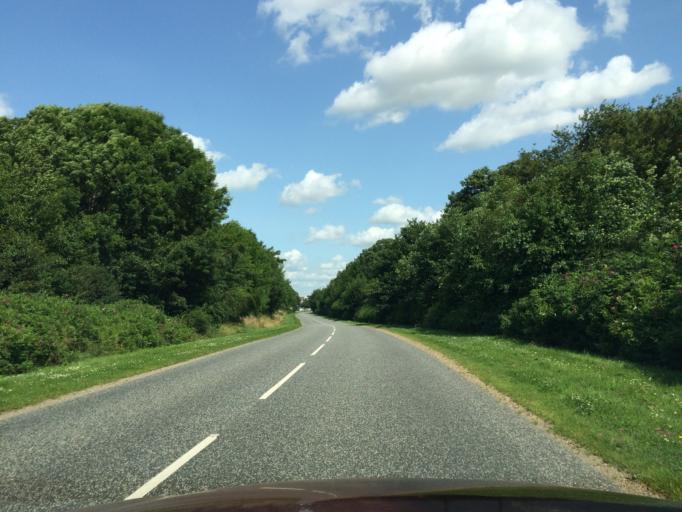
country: DK
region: Central Jutland
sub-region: Viborg Kommune
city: Bjerringbro
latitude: 56.2664
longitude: 9.7209
